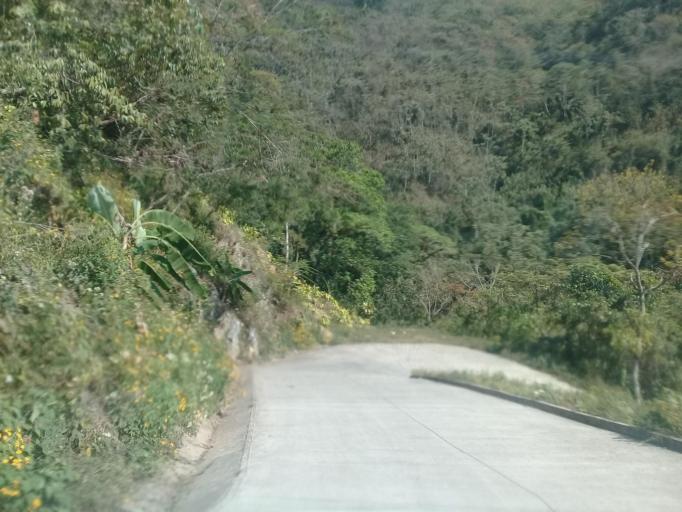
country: MX
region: Veracruz
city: Rafael Delgado
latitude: 18.7830
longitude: -97.0255
